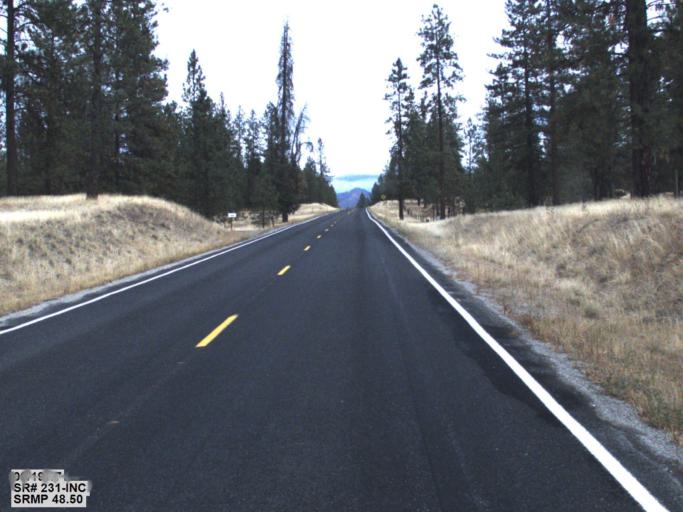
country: US
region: Washington
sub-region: Spokane County
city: Fairchild Air Force Base
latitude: 47.8881
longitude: -117.8330
